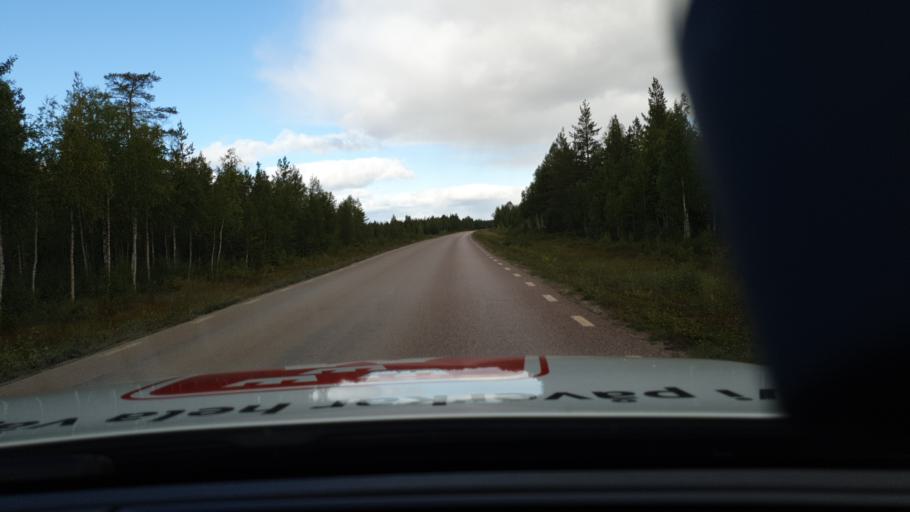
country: SE
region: Norrbotten
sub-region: Pajala Kommun
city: Pajala
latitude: 67.2461
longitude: 22.7799
